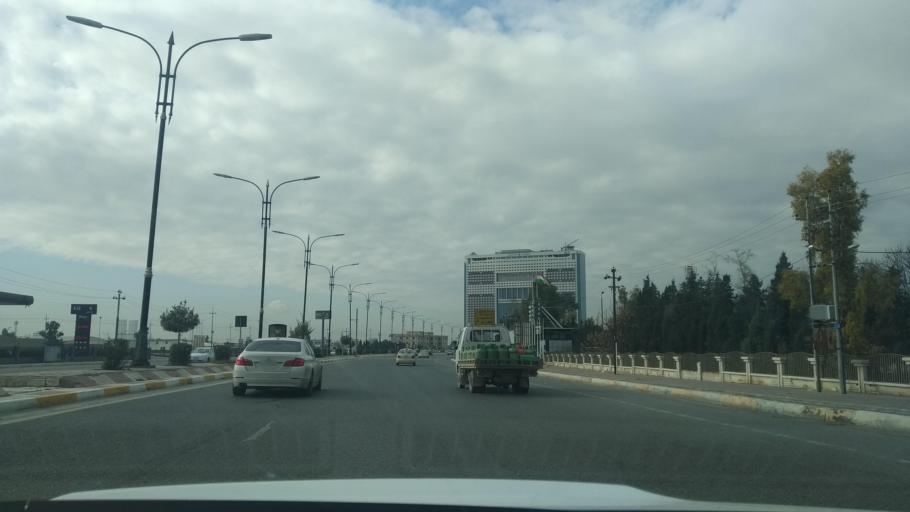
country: IQ
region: Arbil
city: Erbil
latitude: 36.1862
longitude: 43.9872
